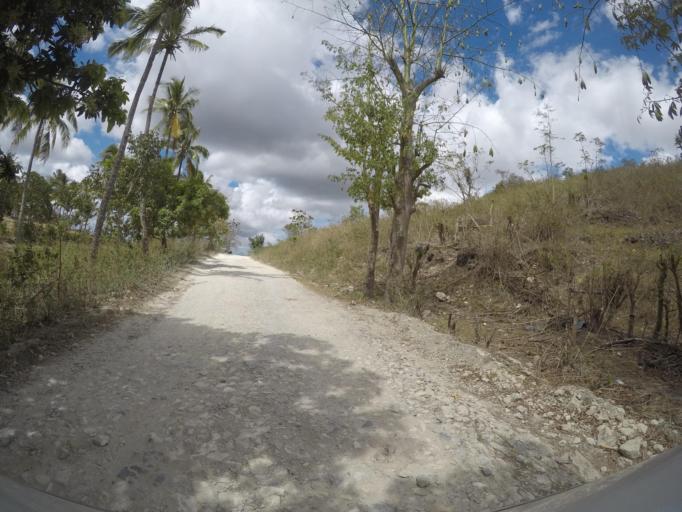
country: TL
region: Baucau
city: Baucau
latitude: -8.5283
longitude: 126.6994
